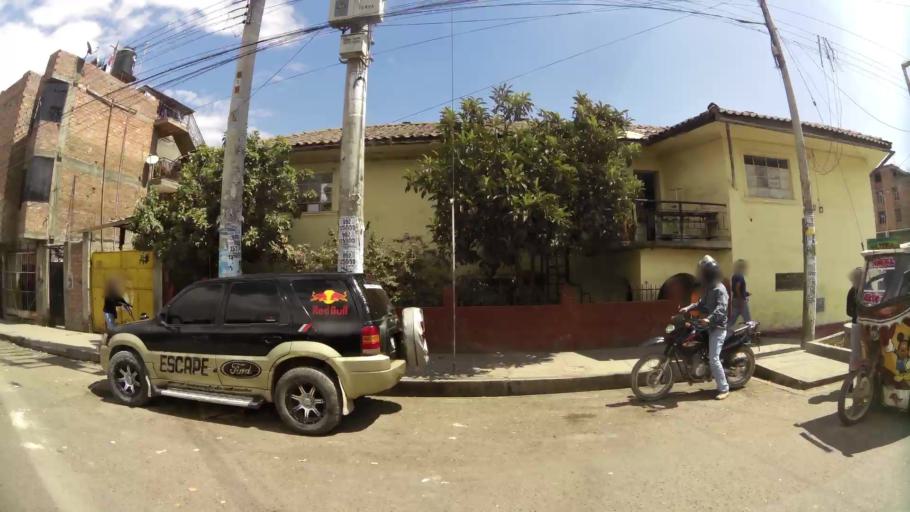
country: PE
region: Junin
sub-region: Provincia de Huancayo
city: Huancayo
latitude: -12.0692
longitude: -75.2008
